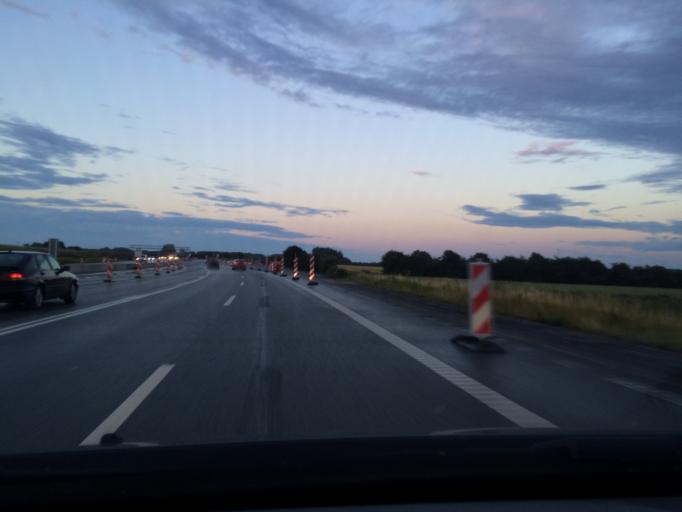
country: DK
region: Zealand
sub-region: Koge Kommune
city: Koge
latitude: 55.4795
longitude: 12.1436
